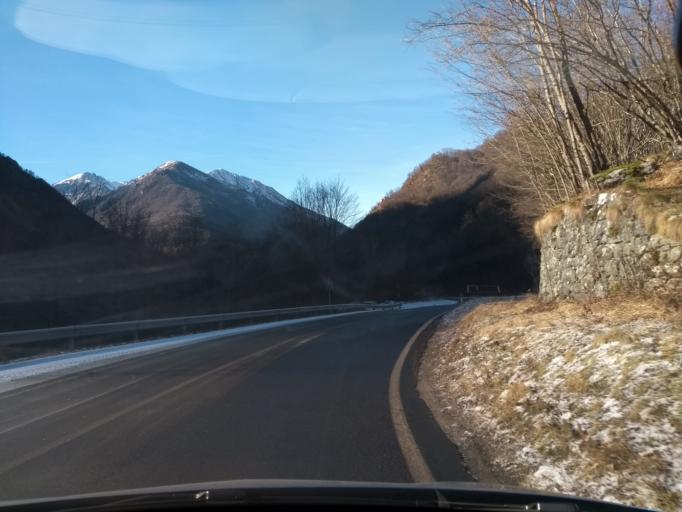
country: IT
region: Piedmont
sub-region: Provincia di Torino
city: Viu
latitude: 45.2264
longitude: 7.3370
